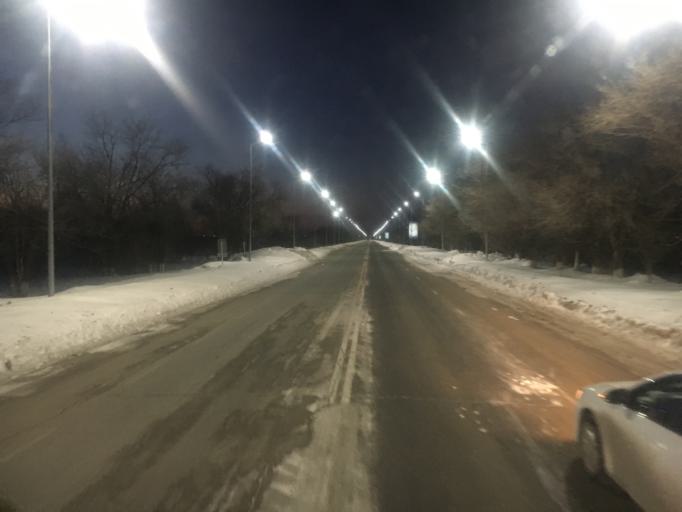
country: KZ
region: Batys Qazaqstan
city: Oral
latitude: 51.1544
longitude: 51.5375
